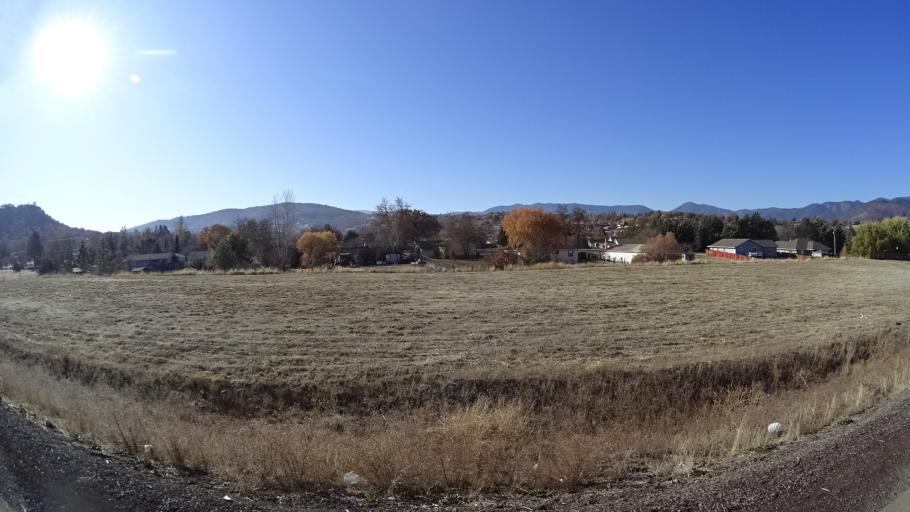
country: US
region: California
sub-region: Siskiyou County
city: Yreka
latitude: 41.7128
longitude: -122.6194
